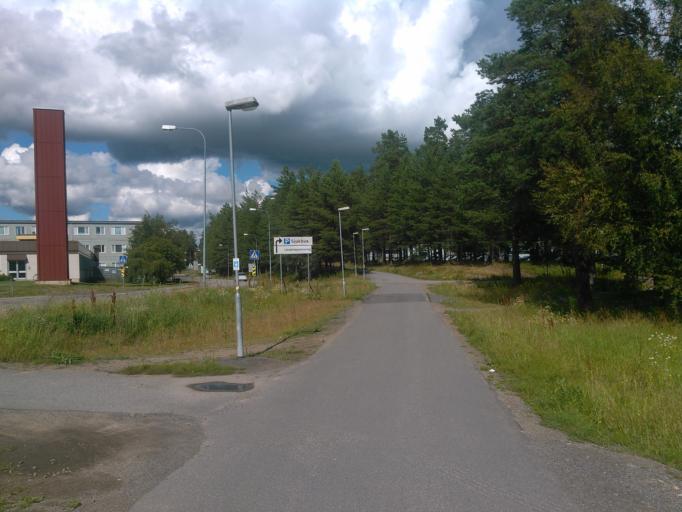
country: SE
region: Vaesterbotten
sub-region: Umea Kommun
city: Umea
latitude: 63.8155
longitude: 20.3038
